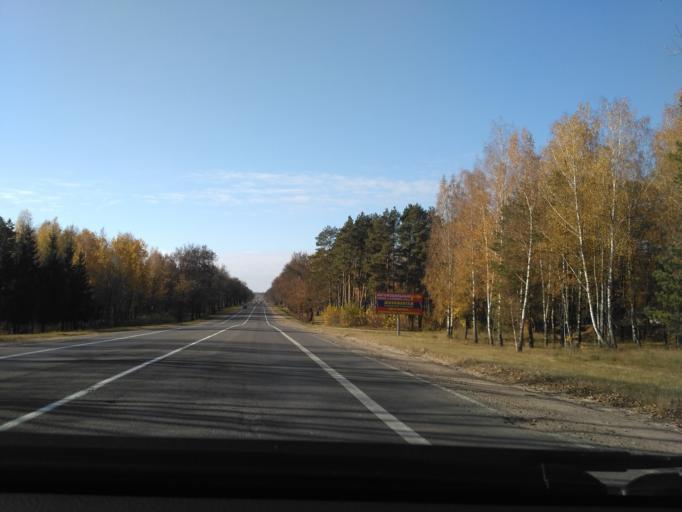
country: BY
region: Minsk
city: Horad Barysaw
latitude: 54.2504
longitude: 28.5559
